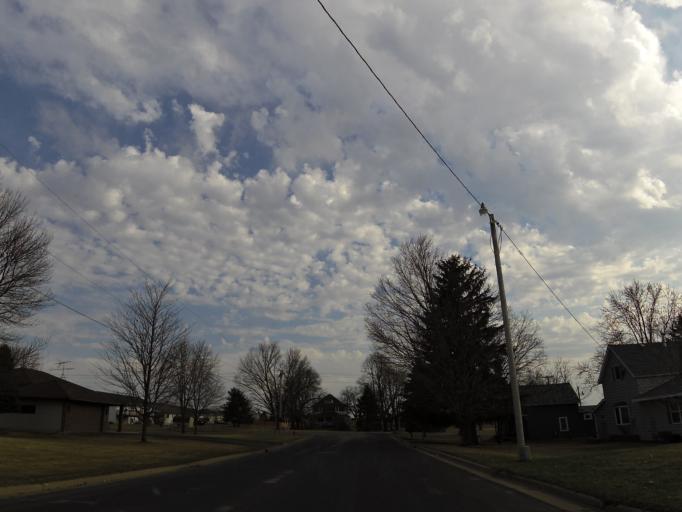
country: US
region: Wisconsin
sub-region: Pierce County
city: Ellsworth
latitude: 44.7184
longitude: -92.4796
